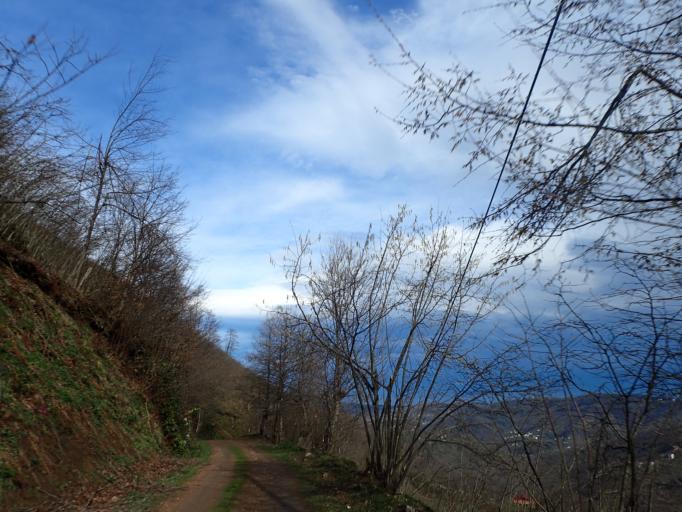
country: TR
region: Ordu
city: Camas
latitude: 40.8869
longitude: 37.5807
